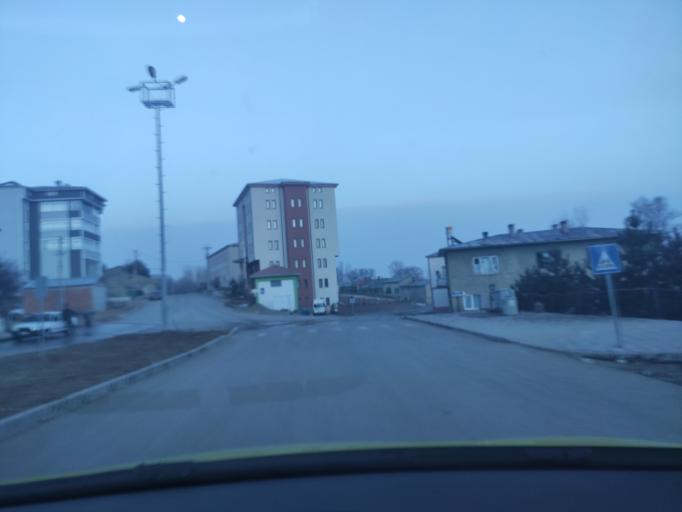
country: TR
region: Bayburt
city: Aydintepe
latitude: 40.3892
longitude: 40.1530
